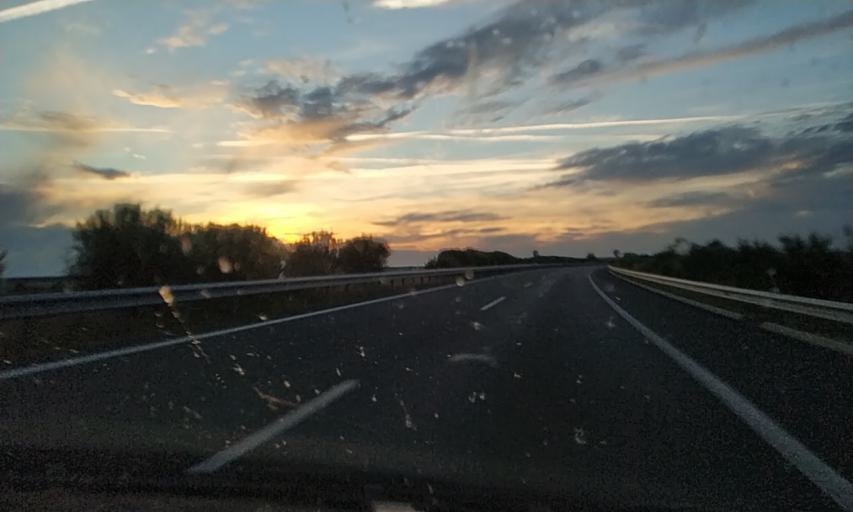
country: ES
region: Extremadura
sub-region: Provincia de Caceres
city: Caceres
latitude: 39.4020
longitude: -6.3942
